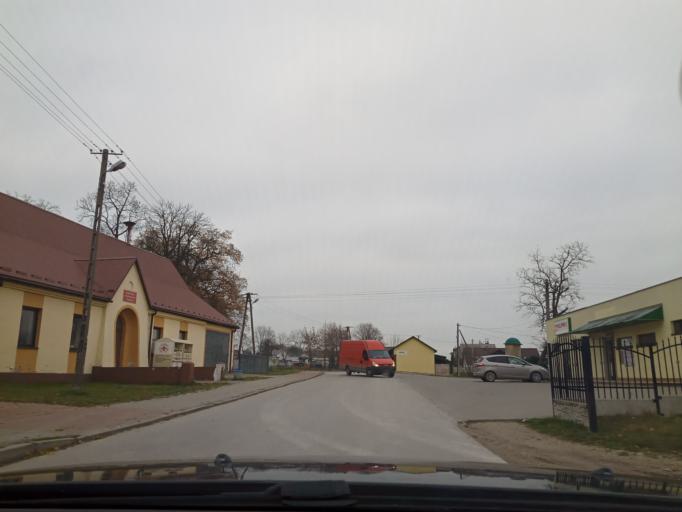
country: PL
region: Swietokrzyskie
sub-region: Powiat jedrzejowski
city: Imielno
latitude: 50.6032
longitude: 20.4911
